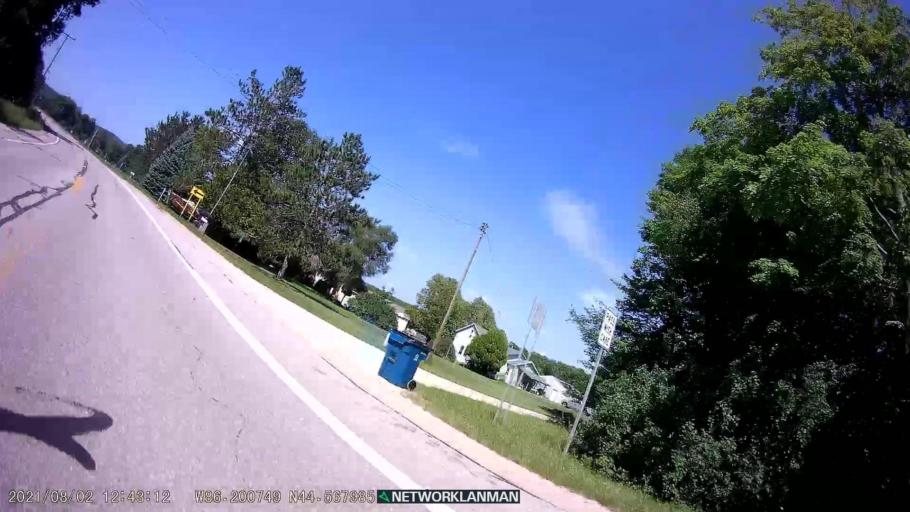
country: US
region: Michigan
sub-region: Benzie County
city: Frankfort
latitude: 44.5683
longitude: -86.2007
